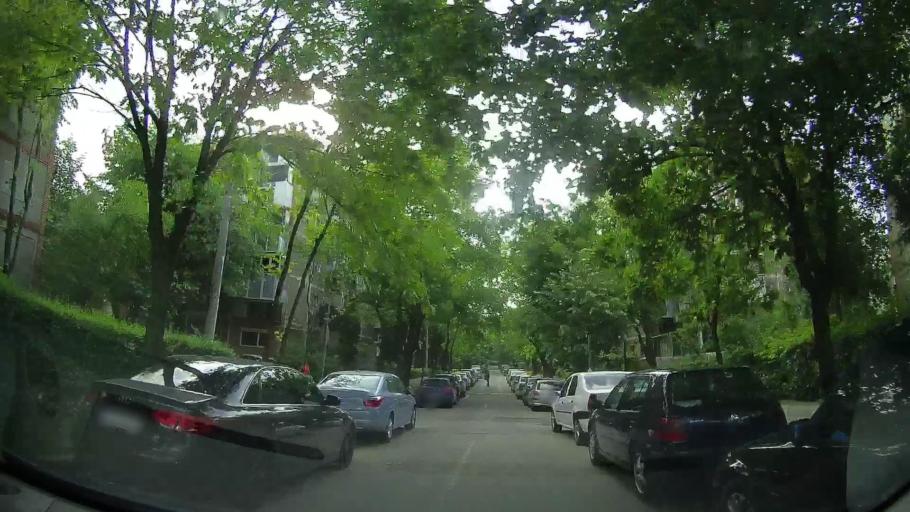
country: RO
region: Timis
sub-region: Comuna Dumbravita
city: Dumbravita
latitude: 45.7769
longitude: 21.2401
